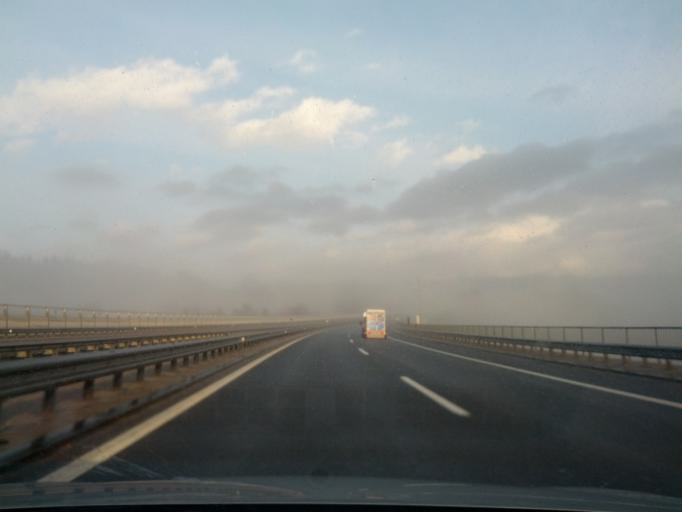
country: SI
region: Naklo
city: Naklo
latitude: 46.2913
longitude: 14.2857
